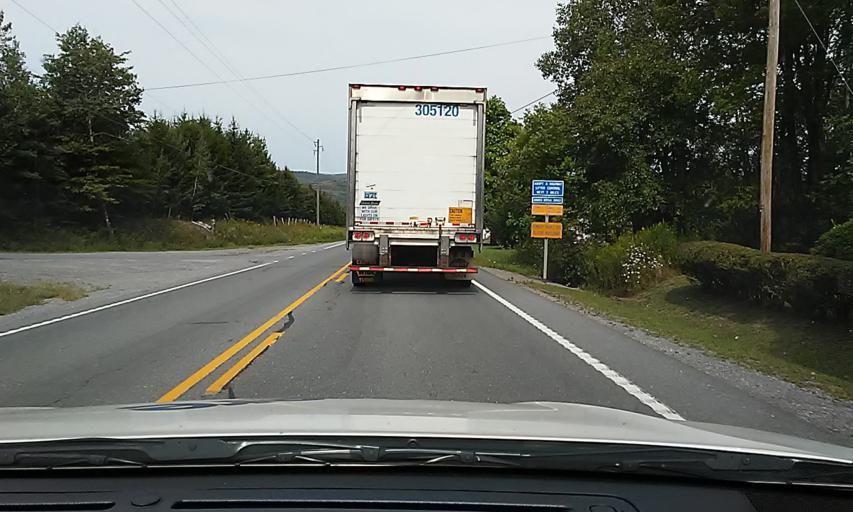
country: US
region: Pennsylvania
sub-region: Clearfield County
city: Treasure Lake
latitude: 41.2659
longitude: -78.6867
